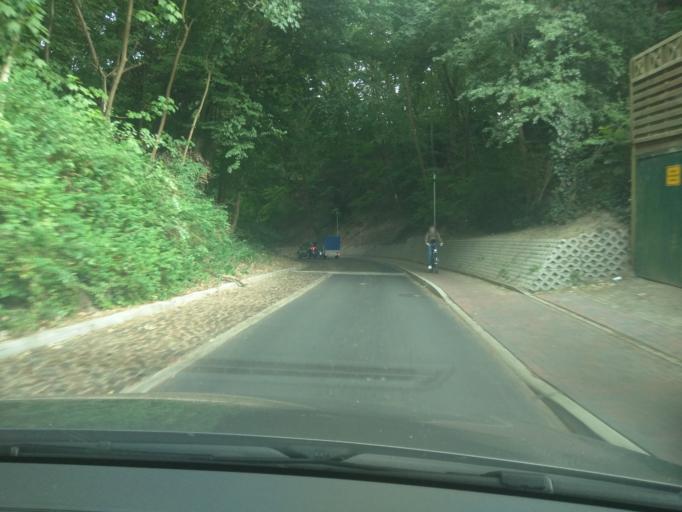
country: DE
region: Schleswig-Holstein
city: Lauenburg
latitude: 53.3737
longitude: 10.5606
